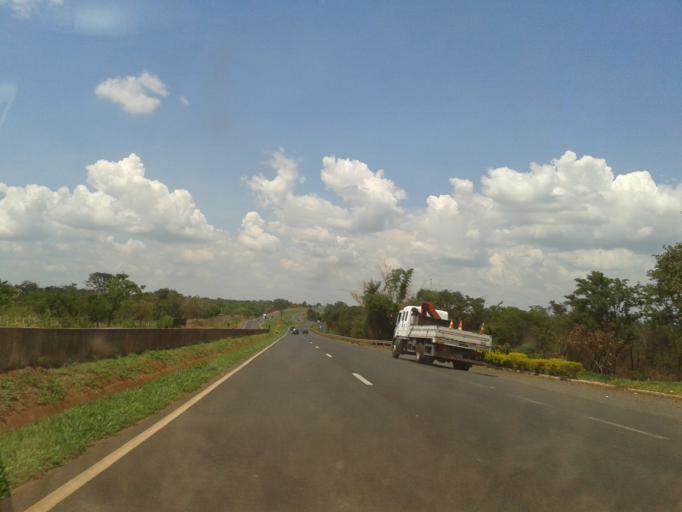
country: BR
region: Minas Gerais
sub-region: Araguari
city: Araguari
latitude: -18.6816
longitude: -48.1789
